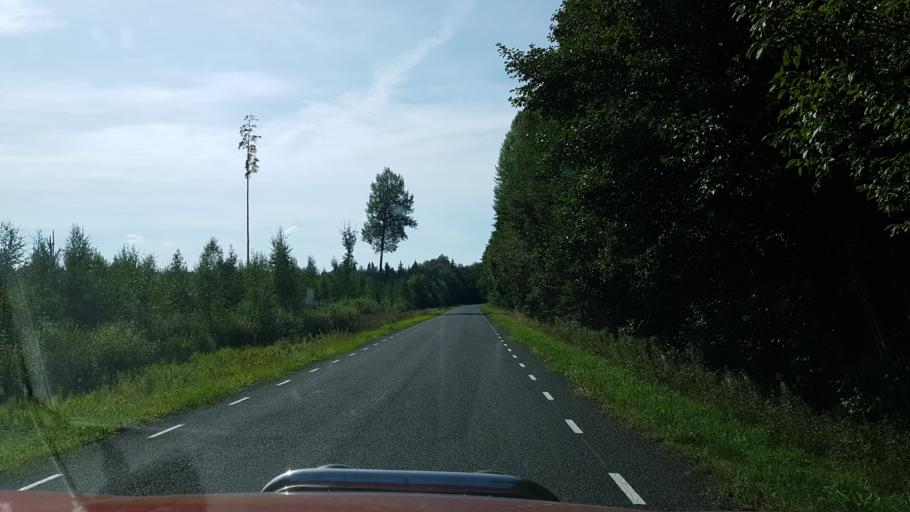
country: EE
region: Viljandimaa
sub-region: Moisakuela linn
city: Moisakula
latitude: 58.3330
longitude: 25.2095
